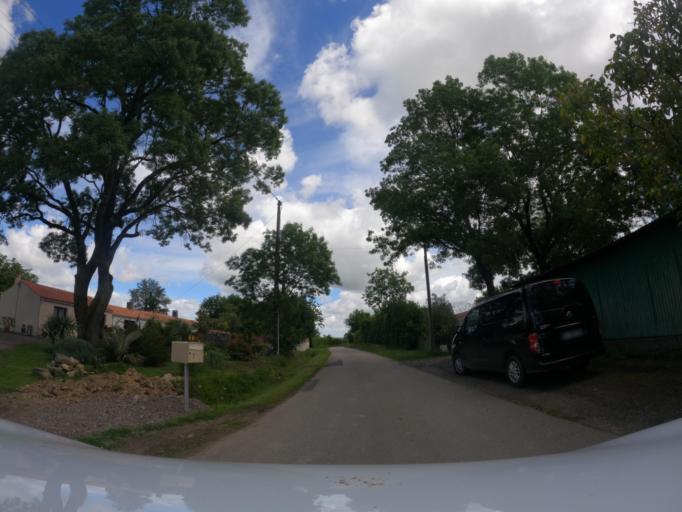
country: FR
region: Pays de la Loire
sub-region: Departement de la Vendee
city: Le Champ-Saint-Pere
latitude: 46.4846
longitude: -1.3544
